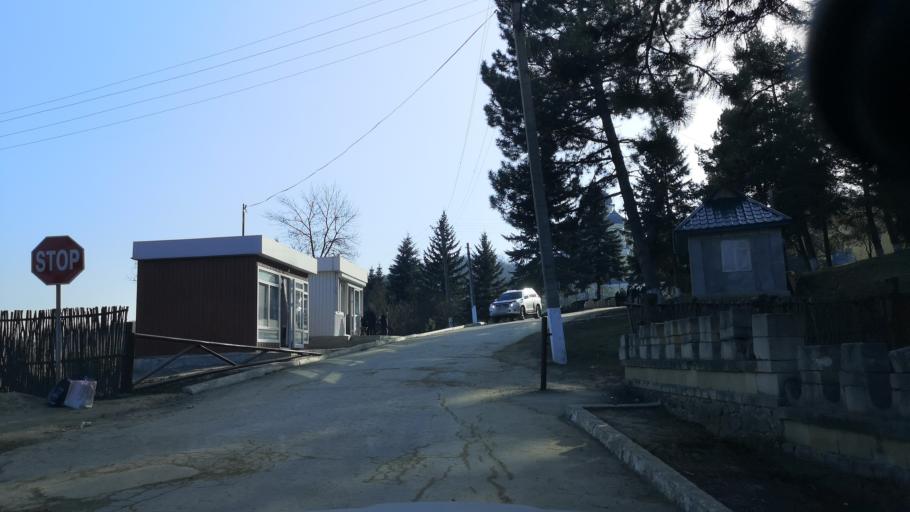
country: MD
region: Nisporeni
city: Nisporeni
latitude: 47.0806
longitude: 28.3224
